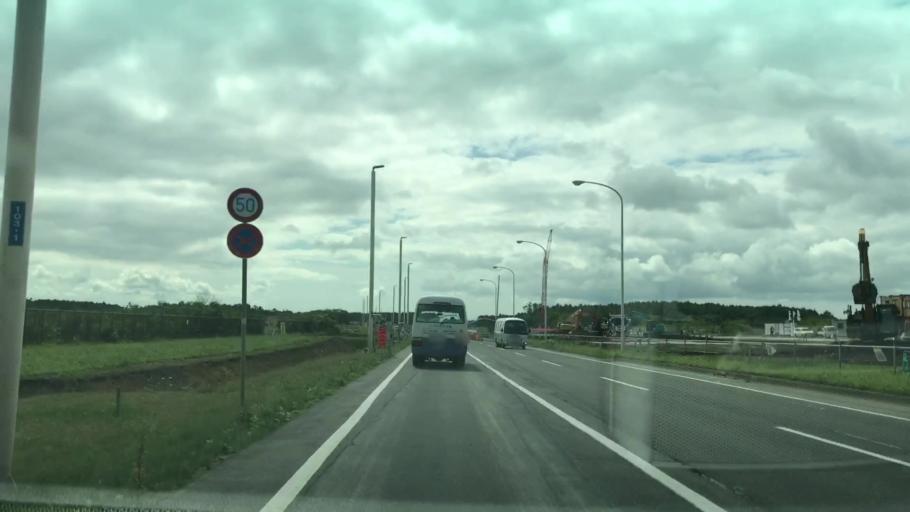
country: JP
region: Hokkaido
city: Chitose
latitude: 42.7794
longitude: 141.6781
